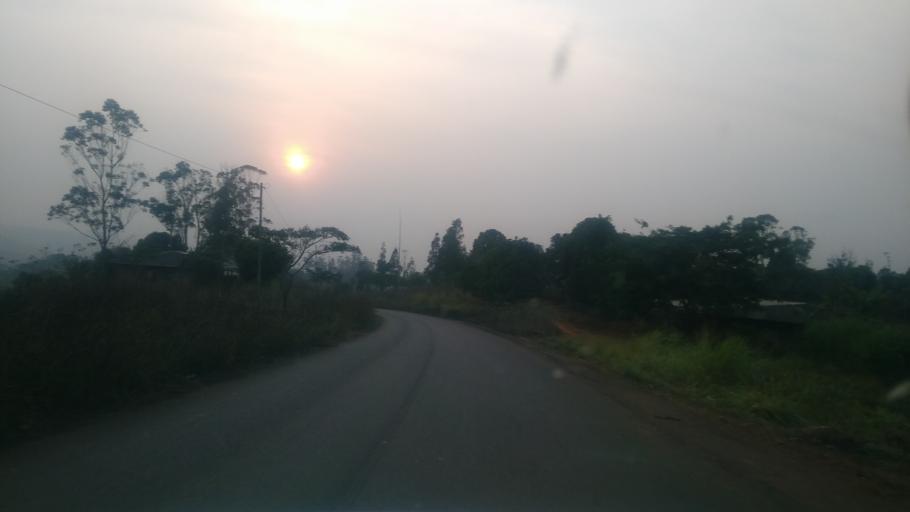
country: CM
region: West
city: Bana
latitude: 5.1641
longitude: 10.2508
